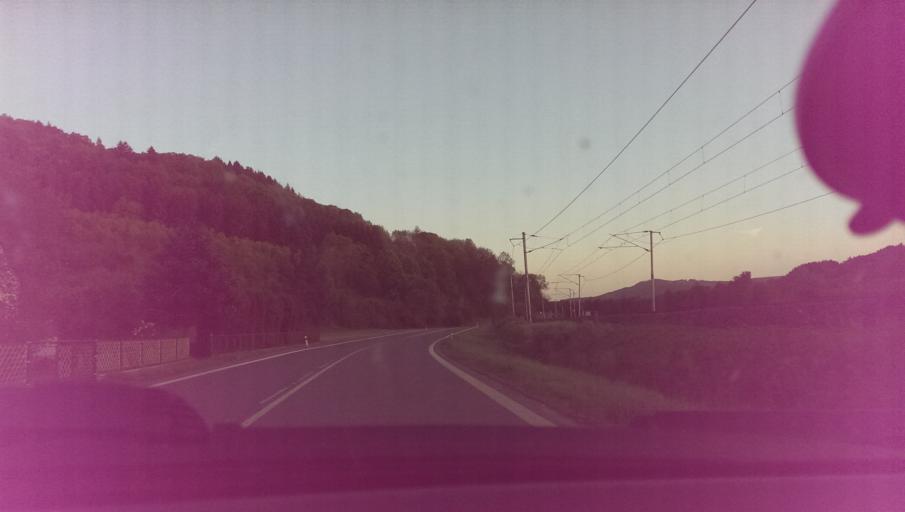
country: CZ
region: Zlin
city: Jablunka
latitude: 49.4077
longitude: 17.9540
